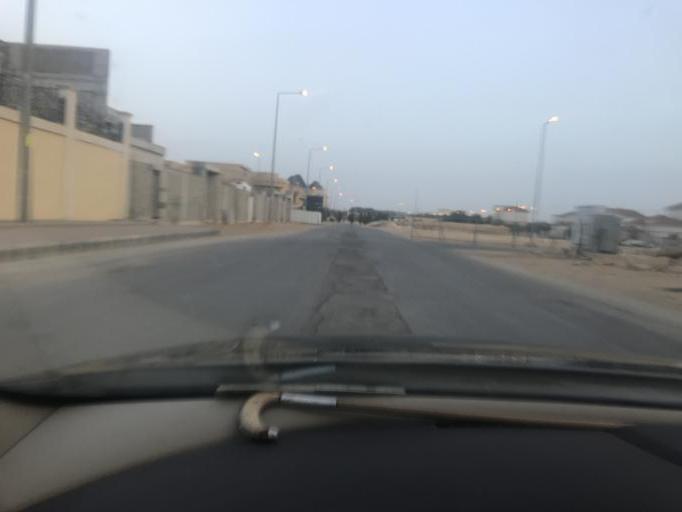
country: SA
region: Ar Riyad
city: Riyadh
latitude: 24.7280
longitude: 46.7485
